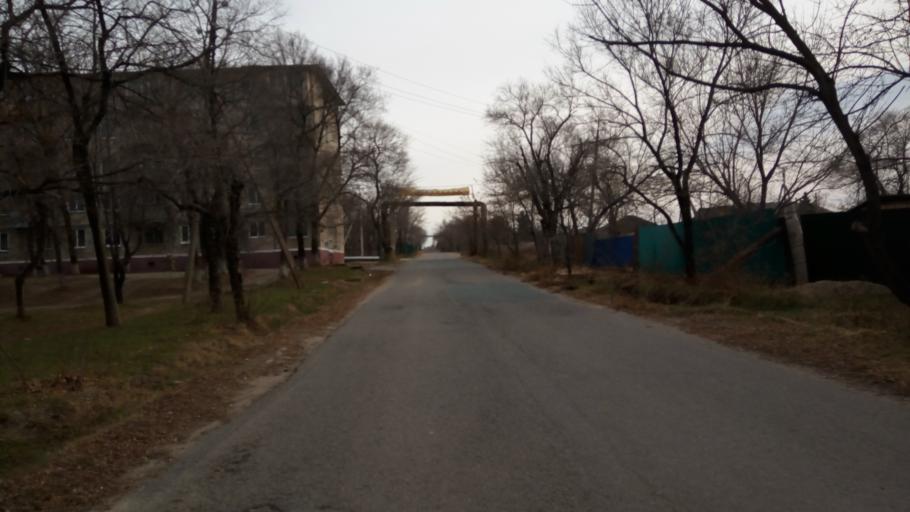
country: RU
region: Primorskiy
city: Novoshakhtinskiy
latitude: 44.0257
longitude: 132.1607
